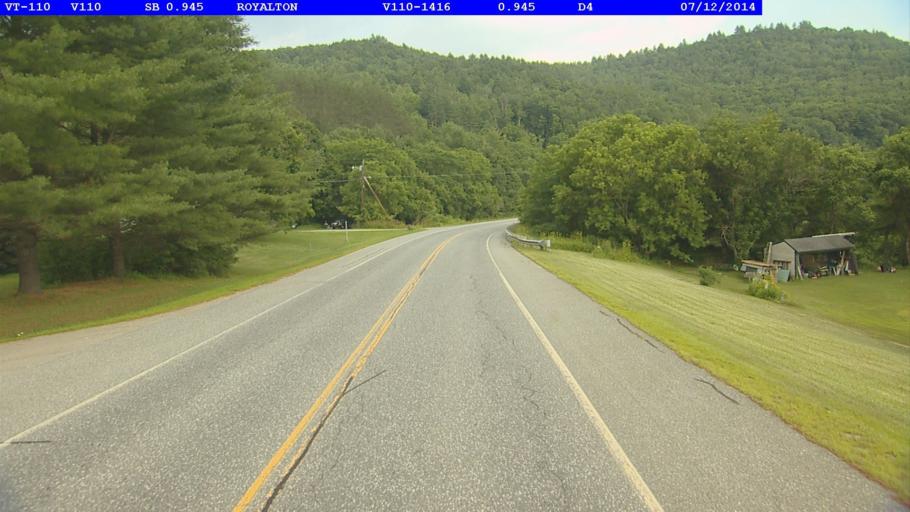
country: US
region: Vermont
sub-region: Orange County
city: Chelsea
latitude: 43.8354
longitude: -72.5128
